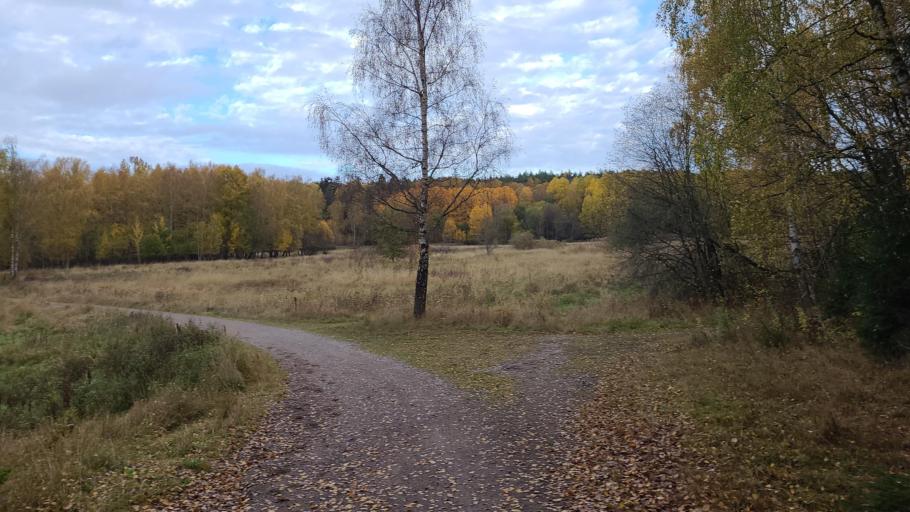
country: SE
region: Stockholm
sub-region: Solna Kommun
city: Rasunda
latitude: 59.3914
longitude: 17.9748
